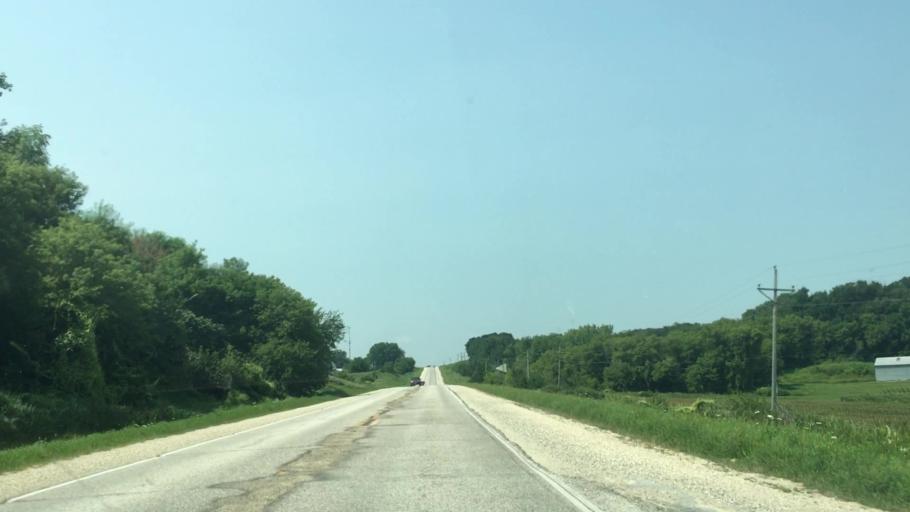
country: US
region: Iowa
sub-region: Fayette County
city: West Union
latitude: 43.0829
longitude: -91.8454
